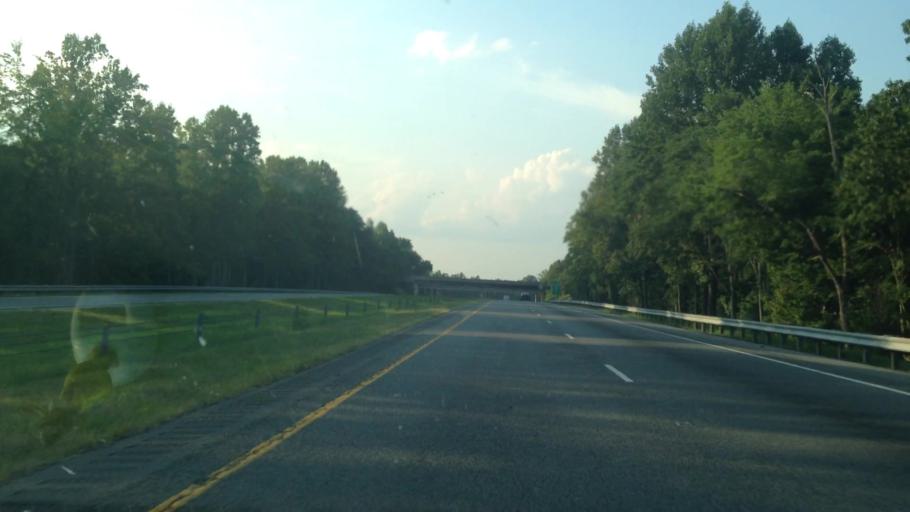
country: US
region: North Carolina
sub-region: Rockingham County
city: Reidsville
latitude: 36.4308
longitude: -79.5725
